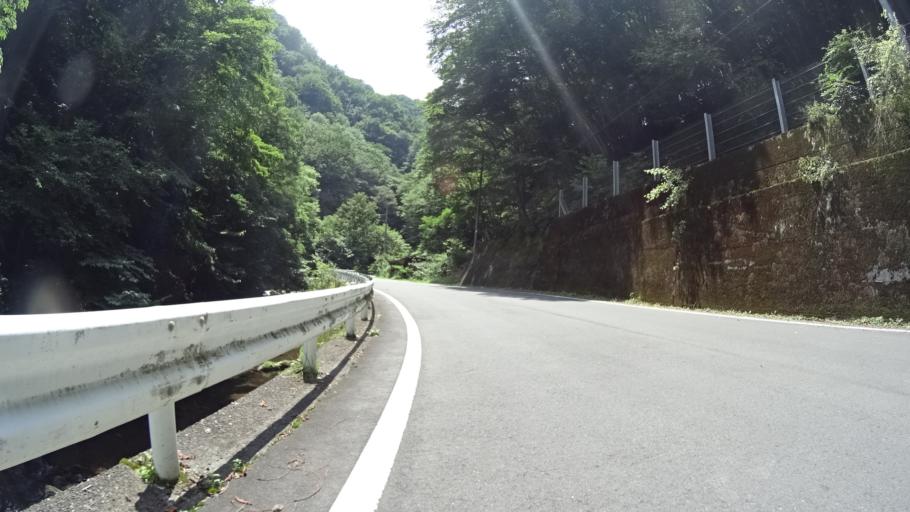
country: JP
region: Nagano
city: Saku
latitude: 36.0694
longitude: 138.7006
